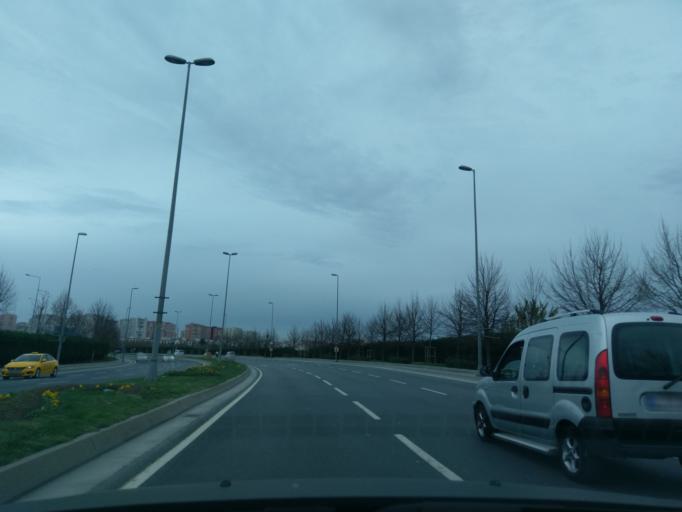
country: TR
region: Istanbul
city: Bahcelievler
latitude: 40.9779
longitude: 28.8400
